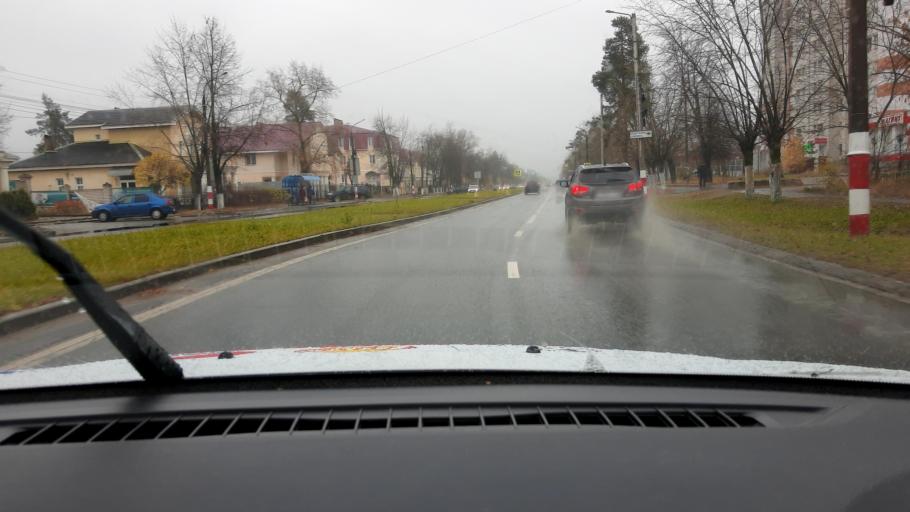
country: RU
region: Nizjnij Novgorod
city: Dzerzhinsk
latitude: 56.2461
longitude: 43.4319
